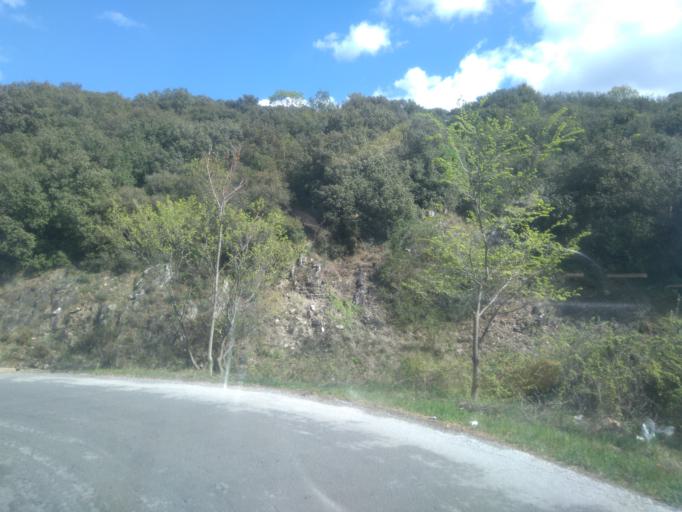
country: GR
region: Central Macedonia
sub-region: Nomos Thessalonikis
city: Asvestochori
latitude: 40.6366
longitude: 23.0159
